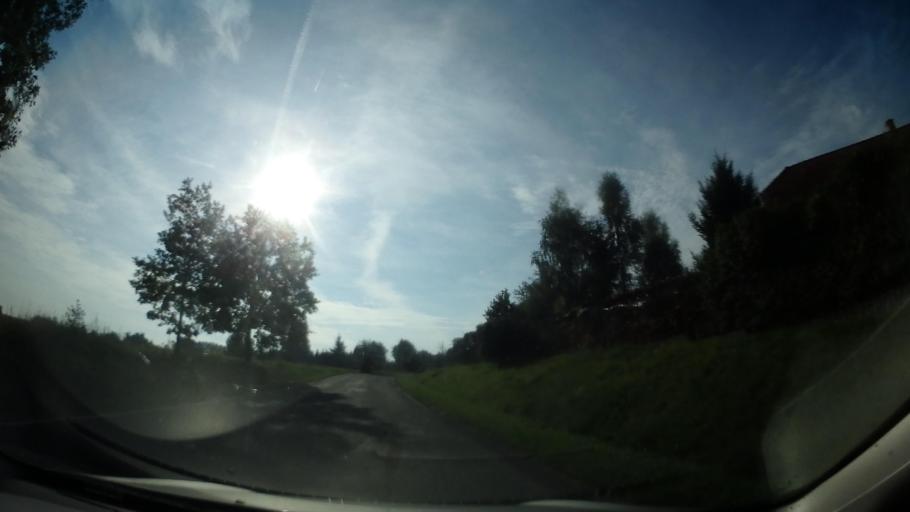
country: CZ
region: Jihocesky
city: Cimelice
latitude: 49.4164
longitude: 14.1175
